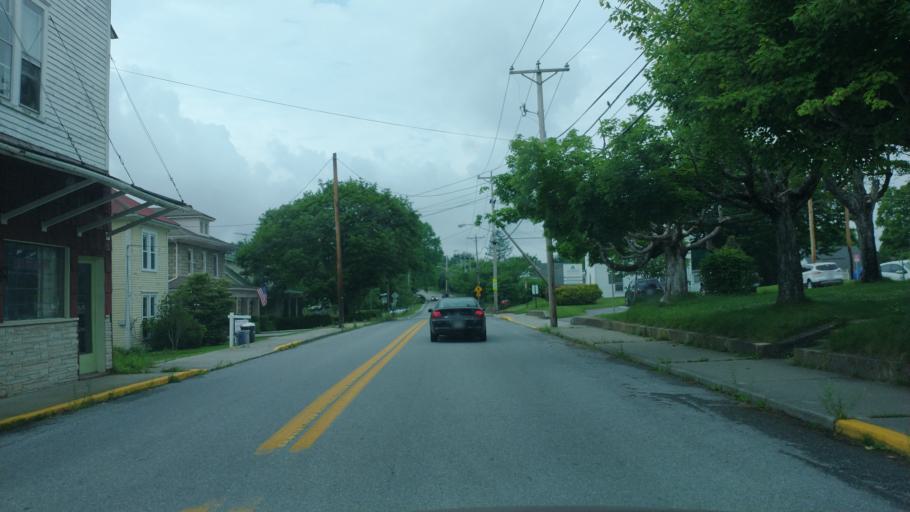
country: US
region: West Virginia
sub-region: Mercer County
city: Athens
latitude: 37.4229
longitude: -81.0092
